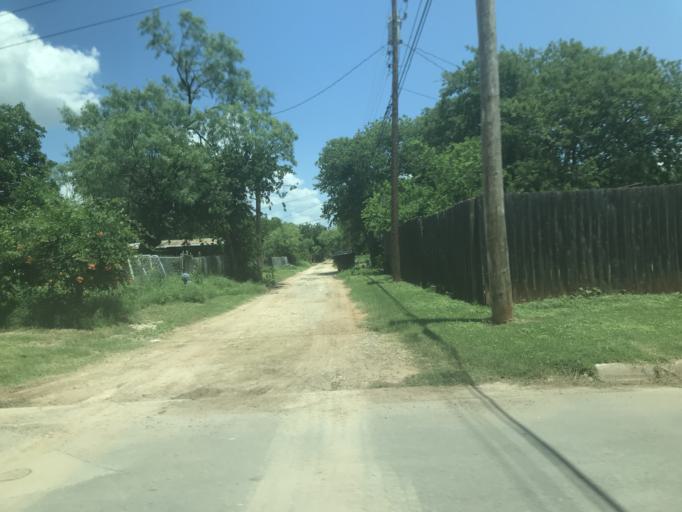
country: US
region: Texas
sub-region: Taylor County
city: Abilene
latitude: 32.4671
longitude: -99.7551
